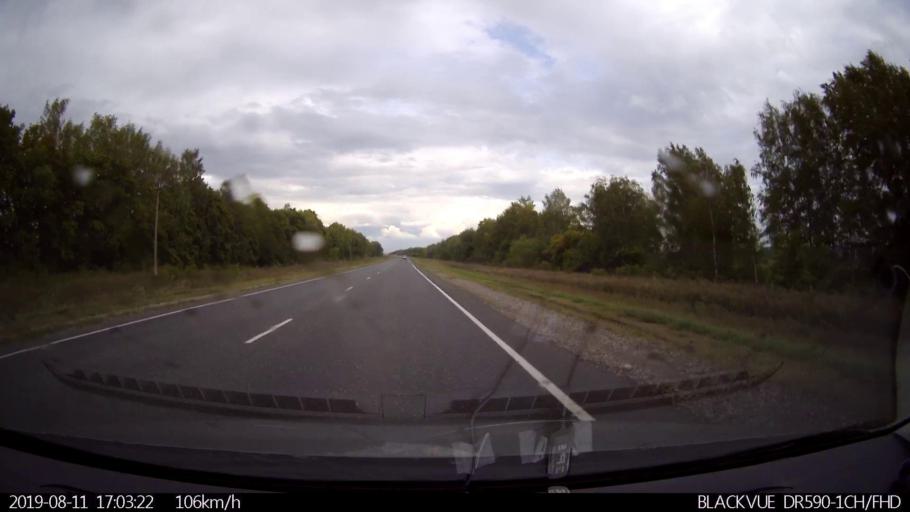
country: RU
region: Ulyanovsk
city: Mayna
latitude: 54.3032
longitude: 47.7380
